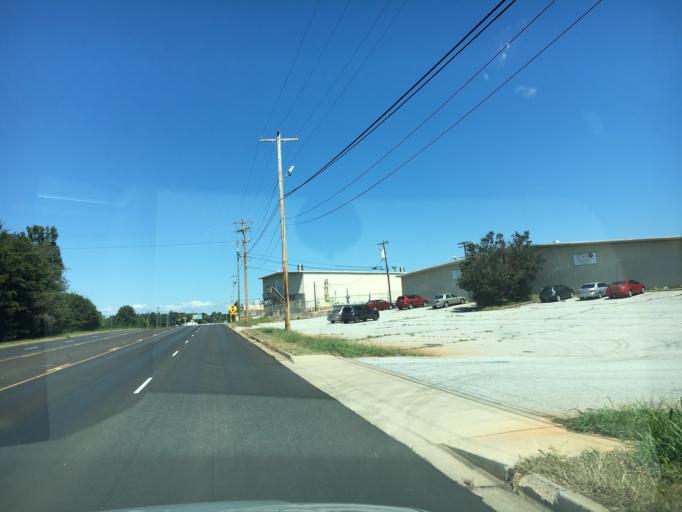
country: US
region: South Carolina
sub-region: Greenville County
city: Gantt
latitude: 34.7964
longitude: -82.4245
